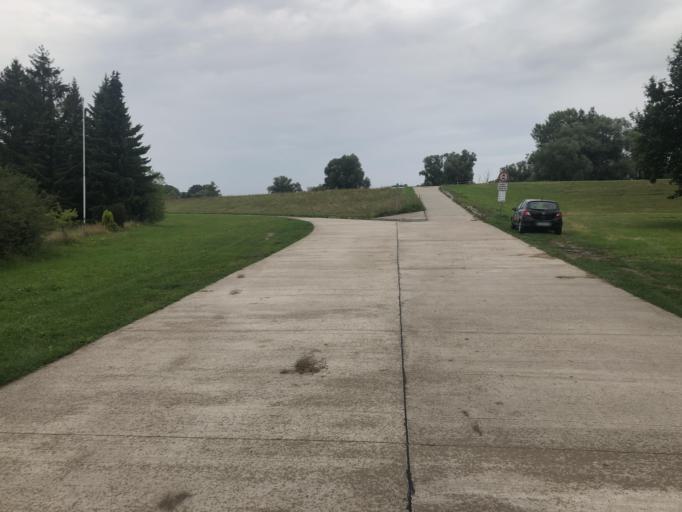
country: DE
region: Mecklenburg-Vorpommern
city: Nostorf
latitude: 53.3628
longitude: 10.6549
